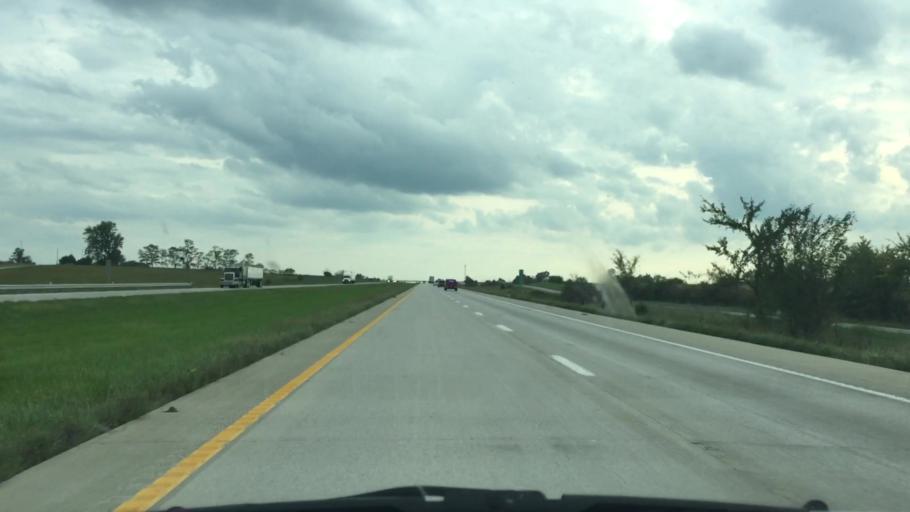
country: US
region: Missouri
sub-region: Clinton County
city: Lathrop
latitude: 39.5972
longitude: -94.2546
